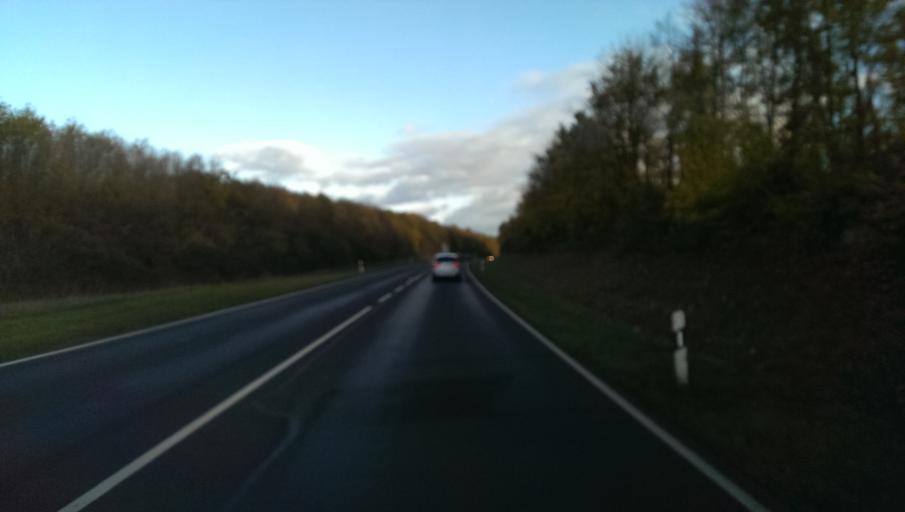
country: DE
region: Bavaria
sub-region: Regierungsbezirk Unterfranken
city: Werneck
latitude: 50.0081
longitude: 10.0621
